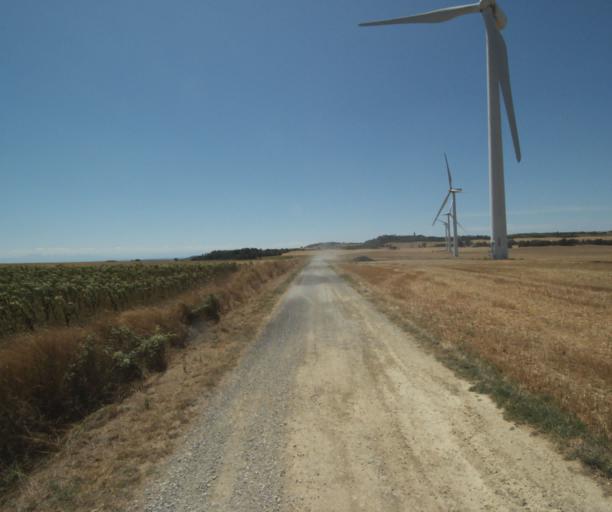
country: FR
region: Midi-Pyrenees
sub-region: Departement de la Haute-Garonne
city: Saint-Felix-Lauragais
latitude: 43.4595
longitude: 1.9133
